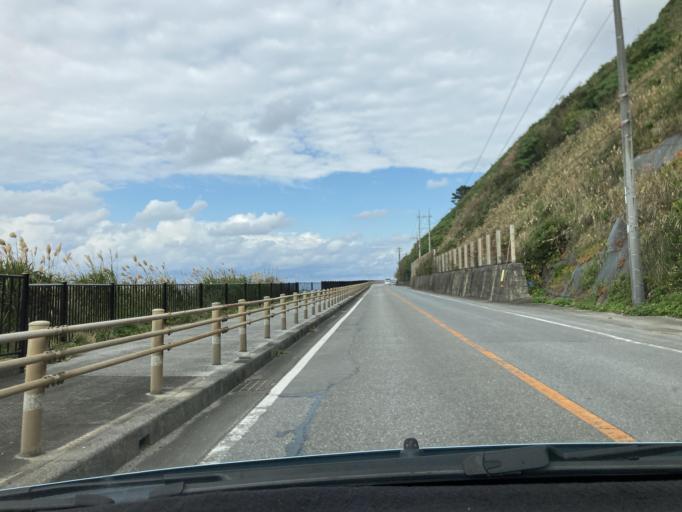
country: JP
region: Okinawa
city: Nago
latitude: 26.7938
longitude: 128.2252
